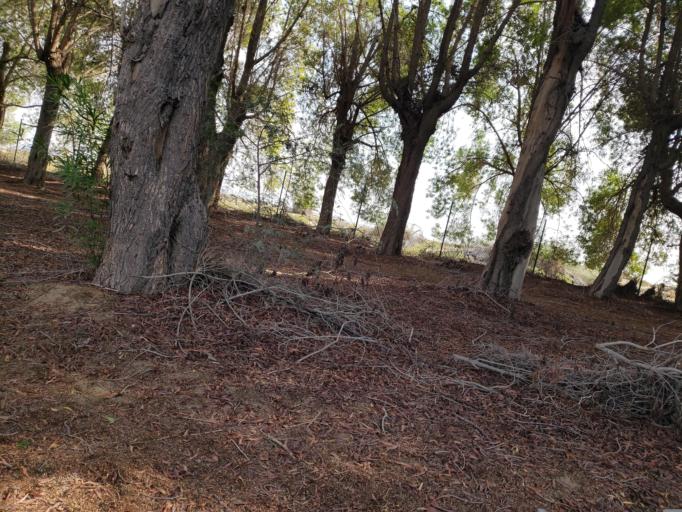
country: AE
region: Dubai
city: Dubai
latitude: 25.1365
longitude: 55.3398
